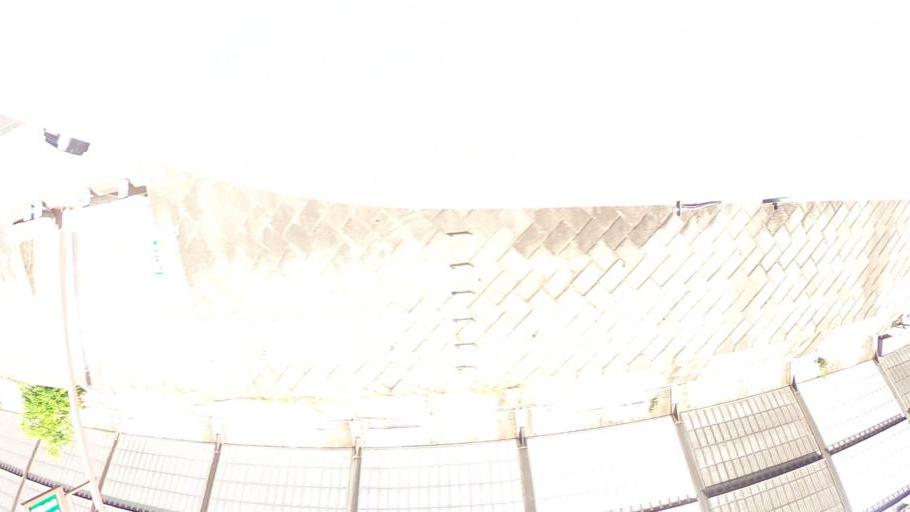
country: JP
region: Saitama
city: Shiki
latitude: 35.7954
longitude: 139.5425
